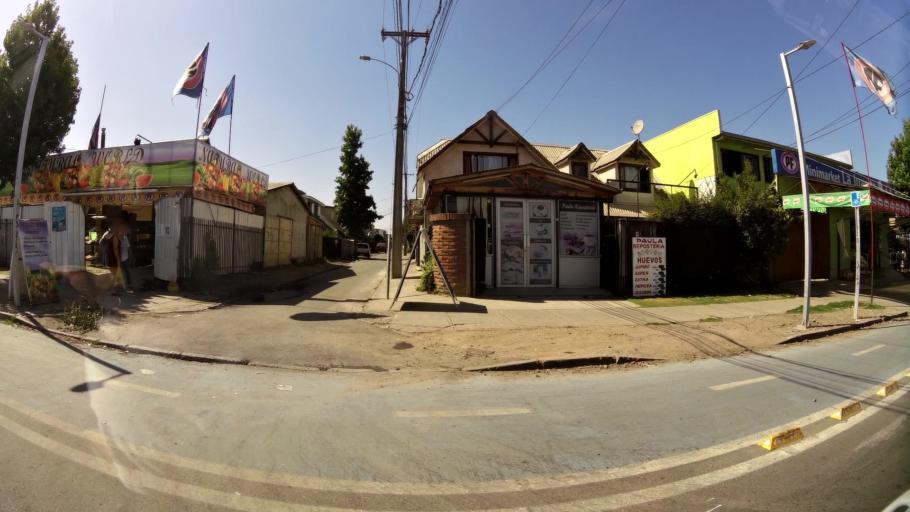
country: CL
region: Maule
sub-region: Provincia de Talca
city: Talca
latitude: -35.4111
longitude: -71.6464
